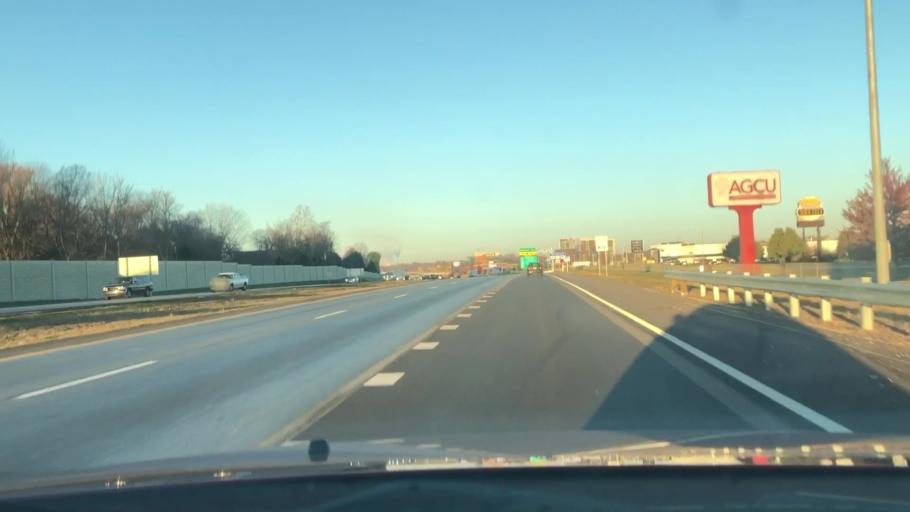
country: US
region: Missouri
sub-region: Greene County
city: Springfield
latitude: 37.1415
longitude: -93.2634
